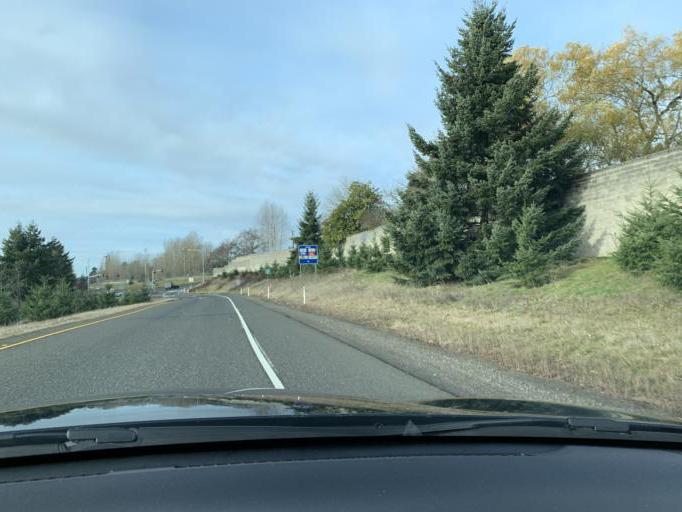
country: US
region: Washington
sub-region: Clark County
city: Mill Plain
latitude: 45.5915
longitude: -122.5018
